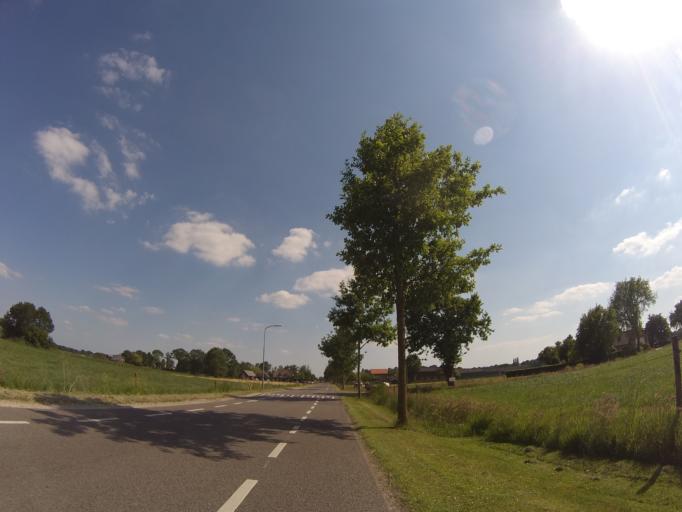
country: NL
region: Gelderland
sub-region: Gemeente Barneveld
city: Terschuur
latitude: 52.1503
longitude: 5.4979
